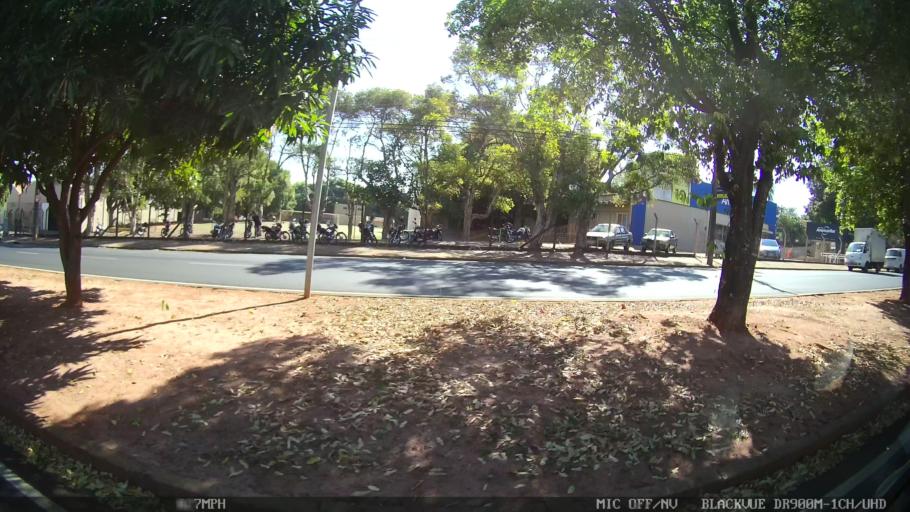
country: BR
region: Sao Paulo
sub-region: Sao Jose Do Rio Preto
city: Sao Jose do Rio Preto
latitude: -20.8107
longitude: -49.4136
